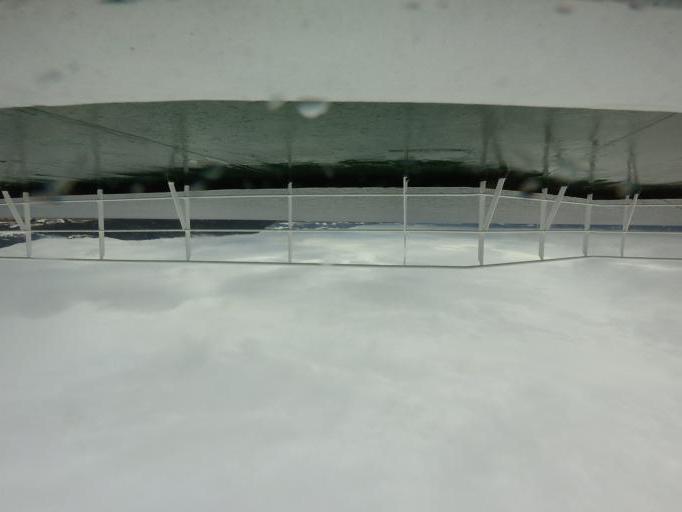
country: NO
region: Sor-Trondelag
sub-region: Skaun
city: Borsa
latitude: 63.4729
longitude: 10.0912
